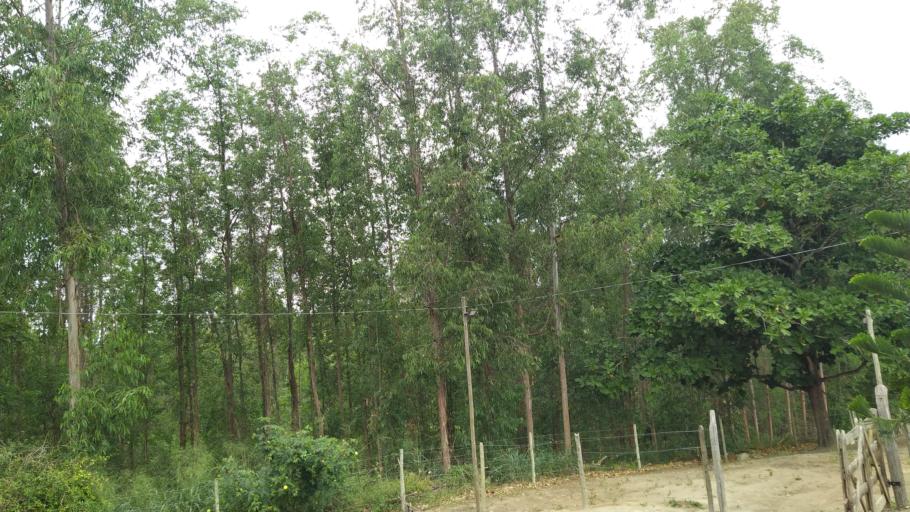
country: BR
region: Minas Gerais
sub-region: Almenara
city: Almenara
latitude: -16.6285
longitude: -40.4569
